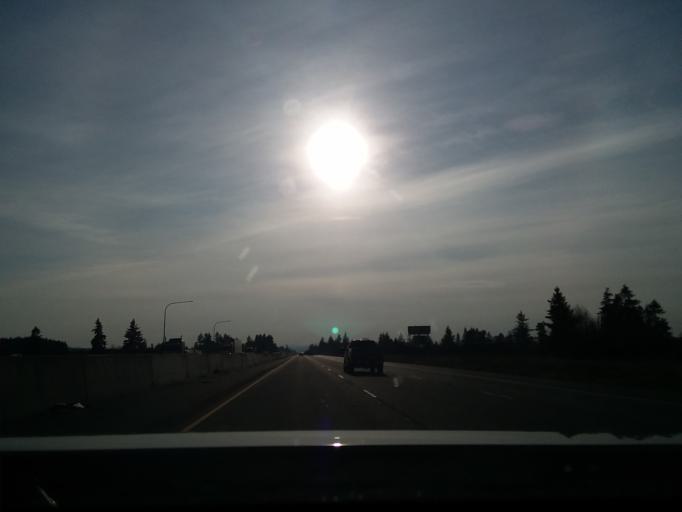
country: US
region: Washington
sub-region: Thurston County
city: Grand Mound
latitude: 46.8458
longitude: -122.9814
